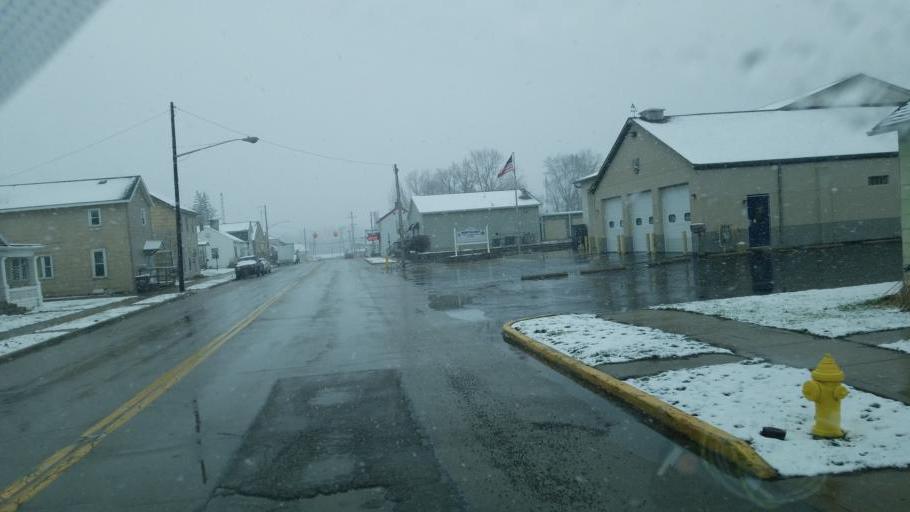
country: US
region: Ohio
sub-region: Preble County
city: New Paris
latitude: 39.8588
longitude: -84.7927
